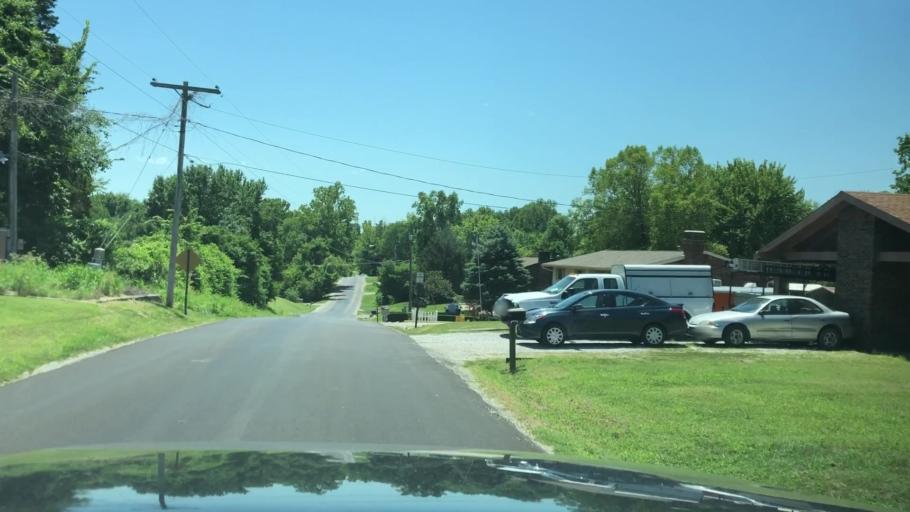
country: US
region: Illinois
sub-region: Saint Clair County
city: Centreville
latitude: 38.5432
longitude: -90.0819
